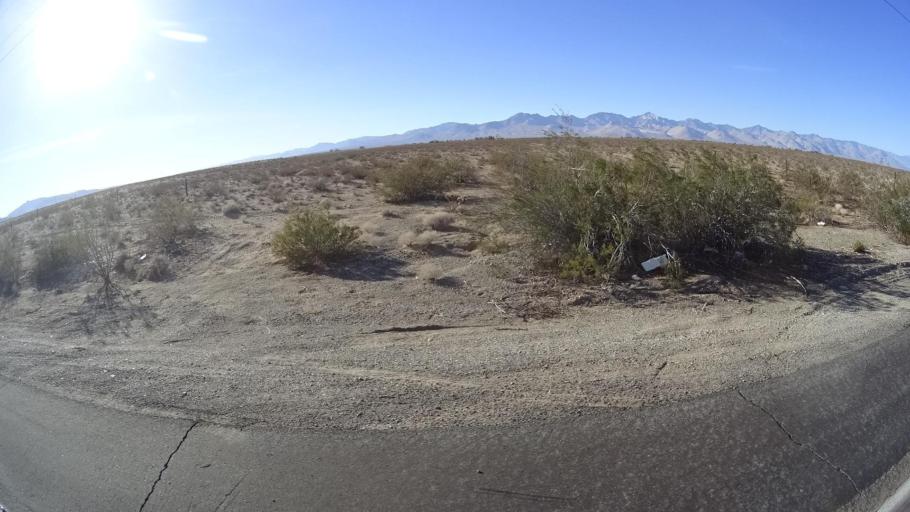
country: US
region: California
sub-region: Kern County
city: China Lake Acres
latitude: 35.6272
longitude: -117.7230
